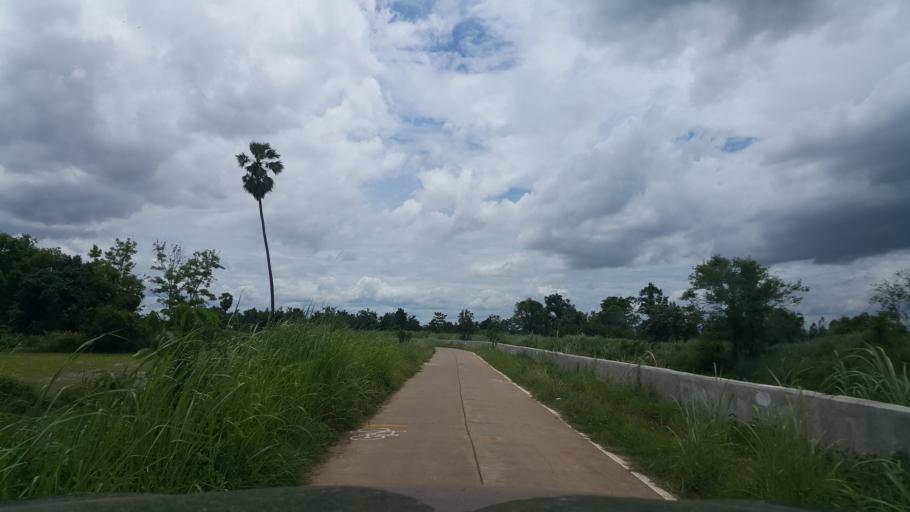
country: TH
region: Sukhothai
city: Sukhothai
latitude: 17.0216
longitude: 99.7995
